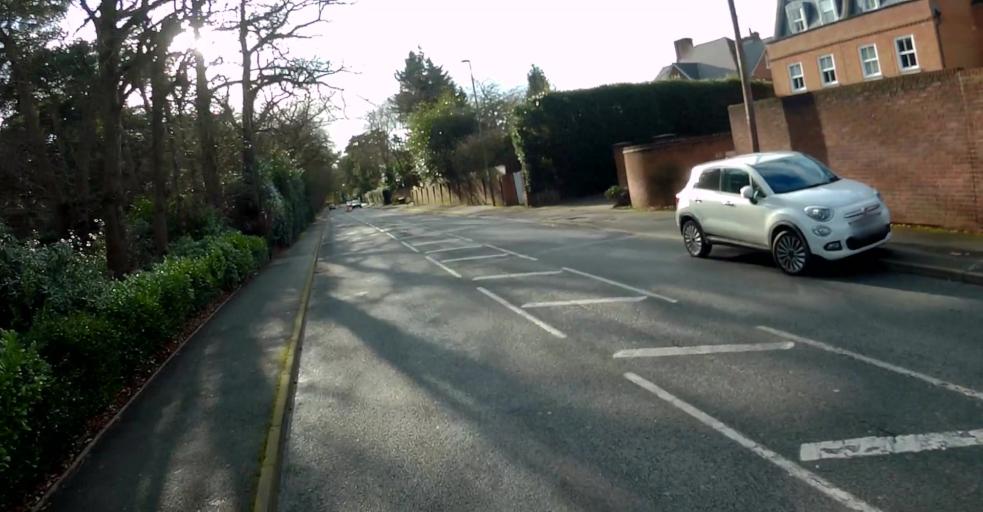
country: GB
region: England
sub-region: Surrey
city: Weybridge
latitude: 51.3656
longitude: -0.4542
